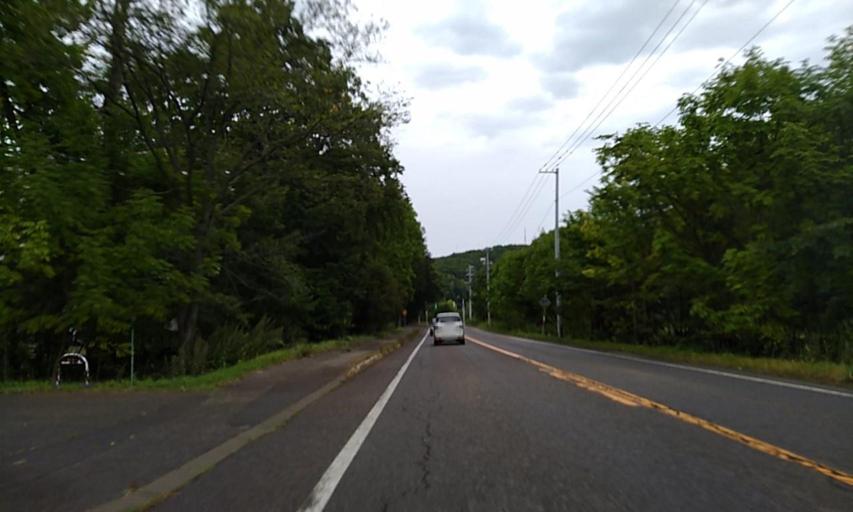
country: JP
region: Hokkaido
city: Abashiri
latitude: 43.9816
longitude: 144.2179
